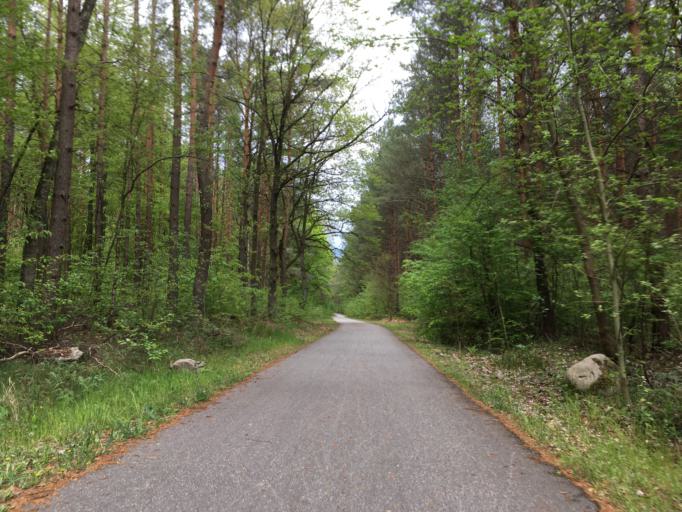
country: DE
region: Brandenburg
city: Bernau bei Berlin
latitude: 52.6896
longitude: 13.5386
